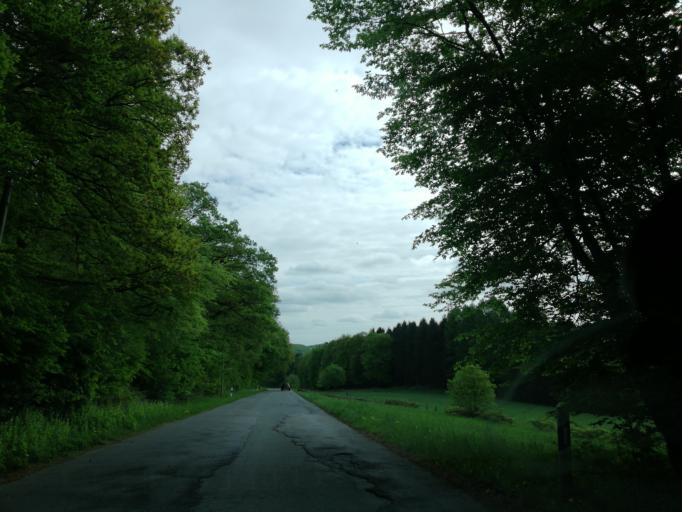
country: DE
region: North Rhine-Westphalia
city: Gevelsberg
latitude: 51.3578
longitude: 7.3027
